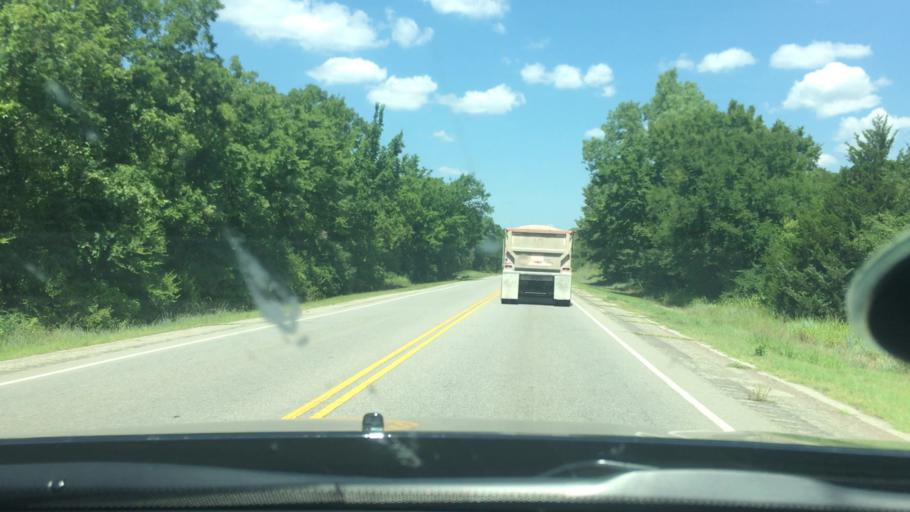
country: US
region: Oklahoma
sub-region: Marshall County
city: Oakland
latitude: 34.1650
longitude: -96.8288
